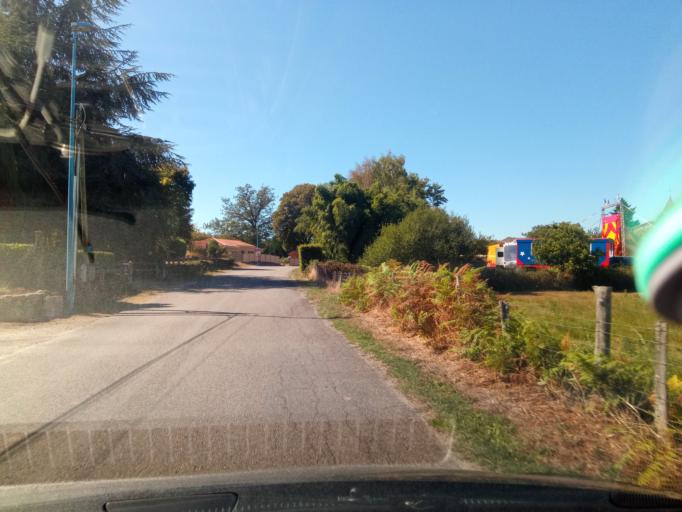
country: FR
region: Limousin
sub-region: Departement de la Haute-Vienne
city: Nantiat
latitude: 46.0782
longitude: 1.2043
